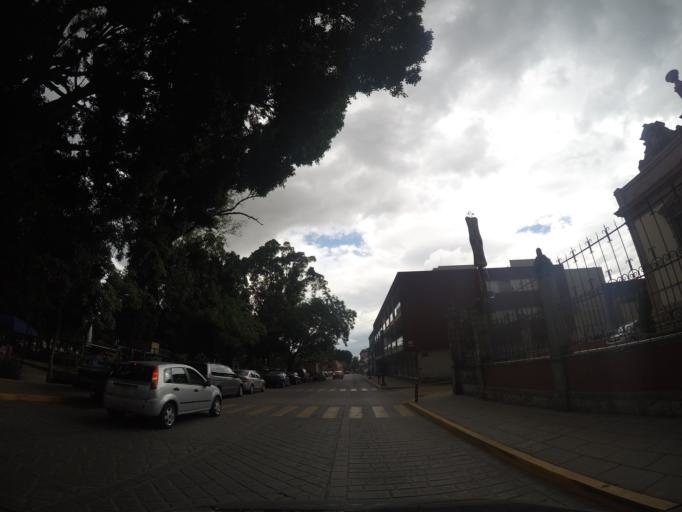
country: MX
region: Oaxaca
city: Oaxaca de Juarez
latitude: 17.0681
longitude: -96.7203
